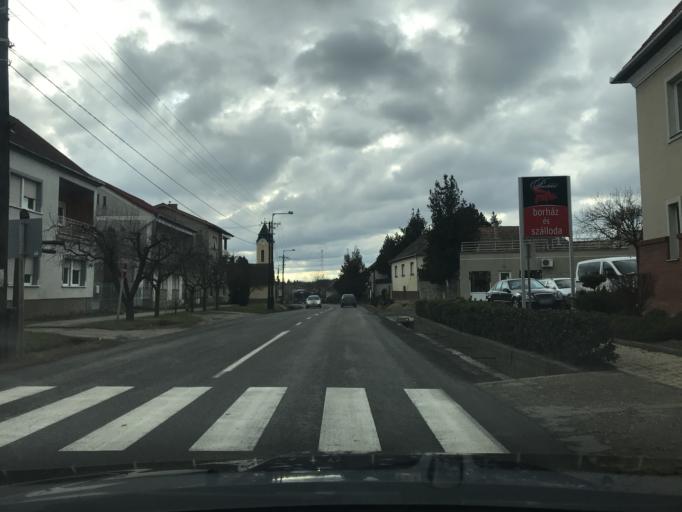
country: HU
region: Bacs-Kiskun
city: Csaszartoltes
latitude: 46.4246
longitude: 19.1790
